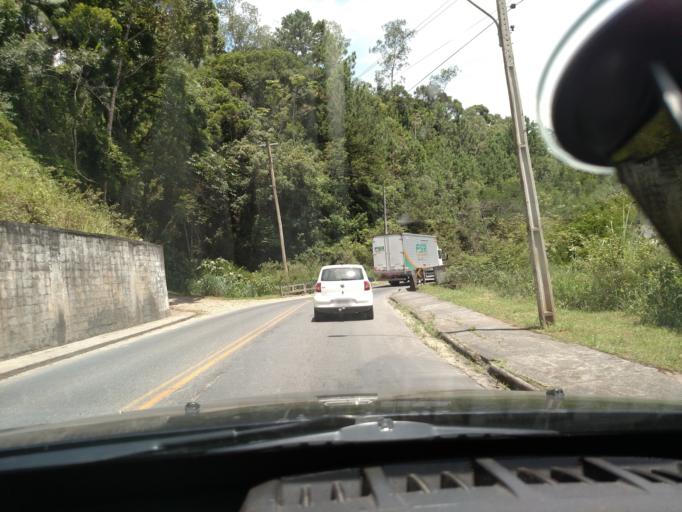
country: BR
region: Santa Catarina
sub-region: Blumenau
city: Blumenau
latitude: -26.9803
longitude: -49.0749
